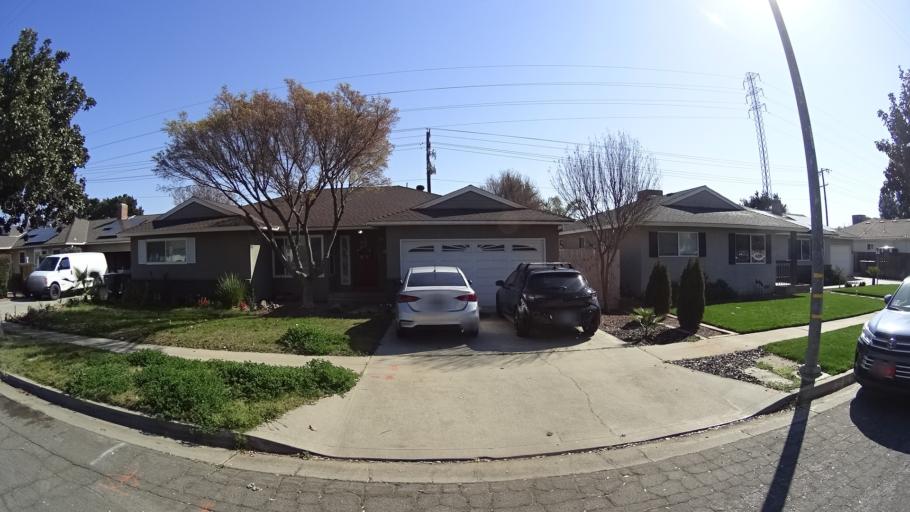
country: US
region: California
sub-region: Fresno County
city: Clovis
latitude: 36.8271
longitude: -119.7685
